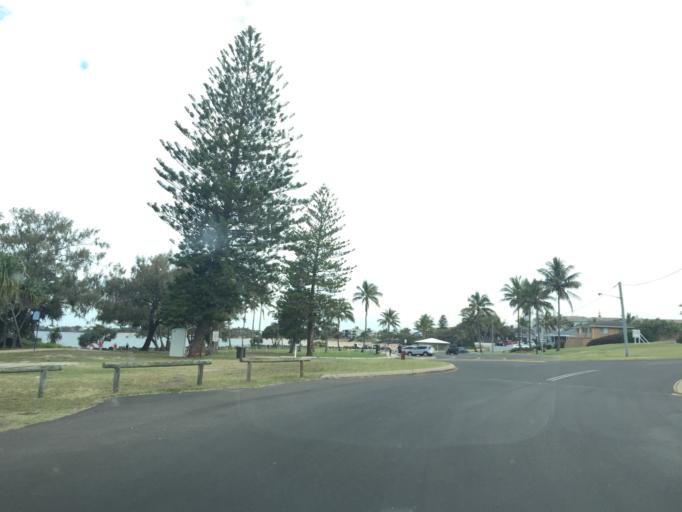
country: AU
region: Queensland
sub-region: Bundaberg
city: Bundaberg
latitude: -24.8171
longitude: 152.4679
